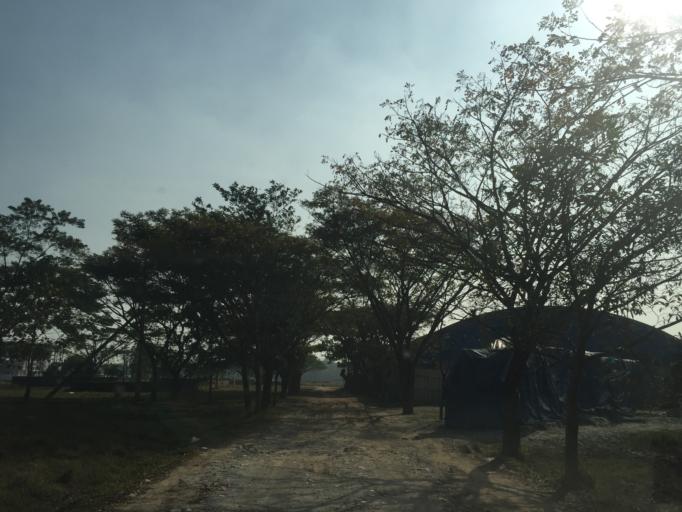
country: BD
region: Dhaka
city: Tungi
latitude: 23.8710
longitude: 90.3128
